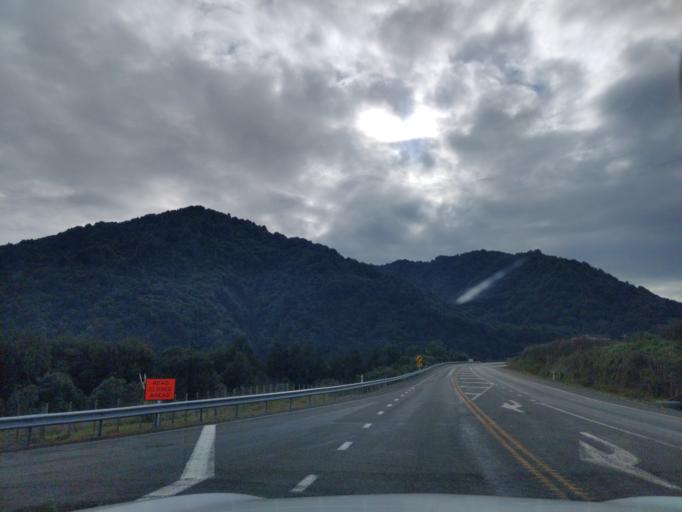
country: NZ
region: Manawatu-Wanganui
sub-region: Palmerston North City
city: Palmerston North
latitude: -40.3366
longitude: 175.8185
